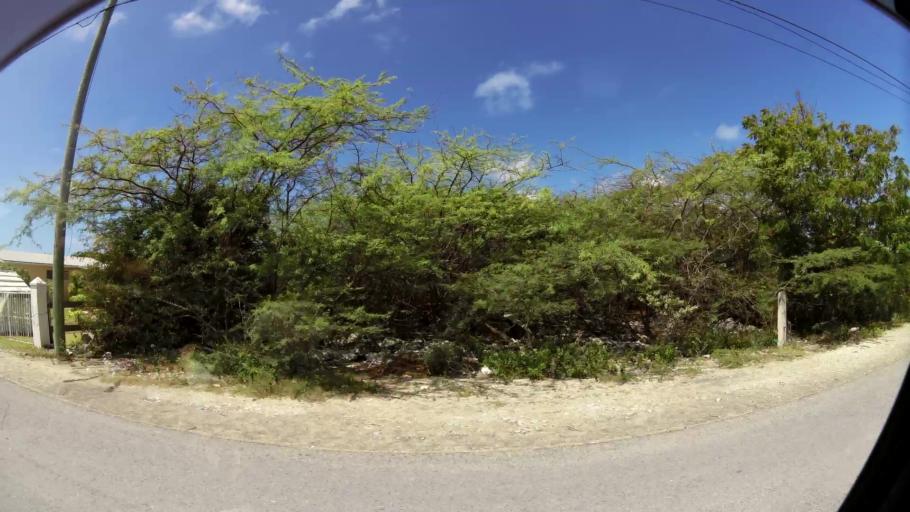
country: TC
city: Cockburn Town
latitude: 21.4817
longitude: -71.1446
